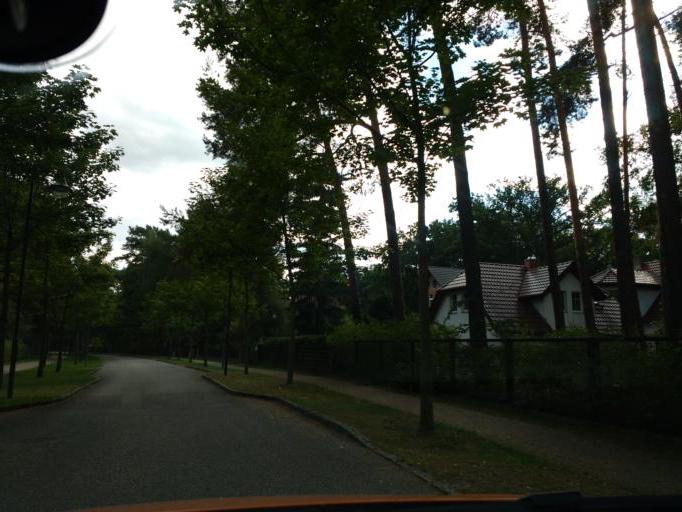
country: DE
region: Brandenburg
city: Bad Saarow
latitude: 52.2732
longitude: 14.0614
